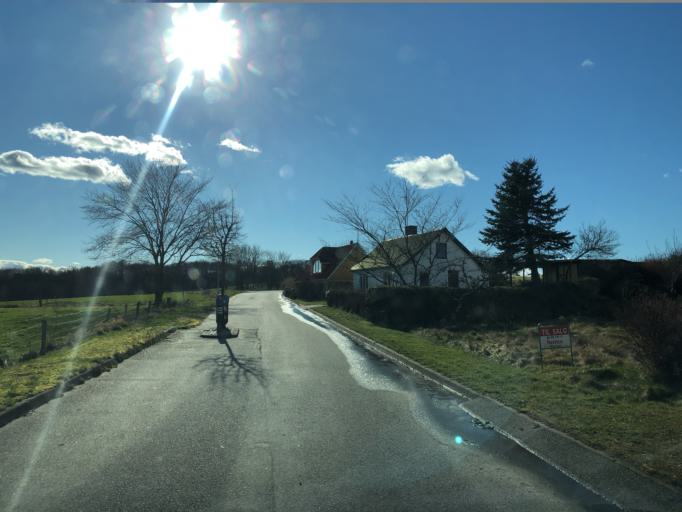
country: DK
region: Central Jutland
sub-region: Randers Kommune
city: Langa
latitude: 56.3255
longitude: 9.9071
